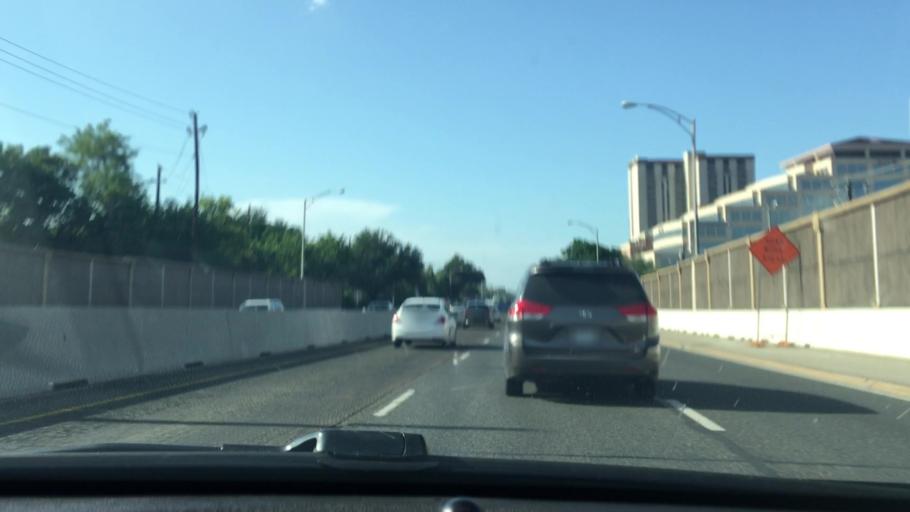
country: US
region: Texas
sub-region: Dallas County
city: University Park
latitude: 32.8599
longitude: -96.8121
